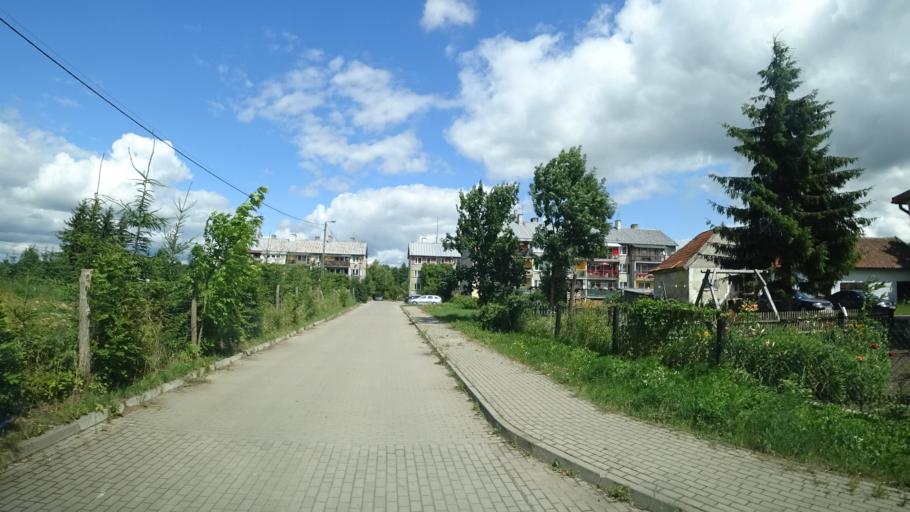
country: PL
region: Warmian-Masurian Voivodeship
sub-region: Powiat goldapski
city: Banie Mazurskie
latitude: 54.2178
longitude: 22.1539
